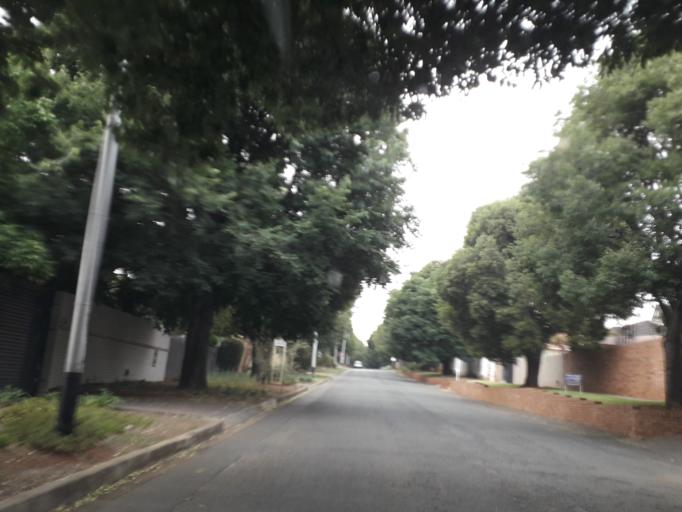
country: ZA
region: Gauteng
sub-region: City of Johannesburg Metropolitan Municipality
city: Johannesburg
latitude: -26.1380
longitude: 27.9869
